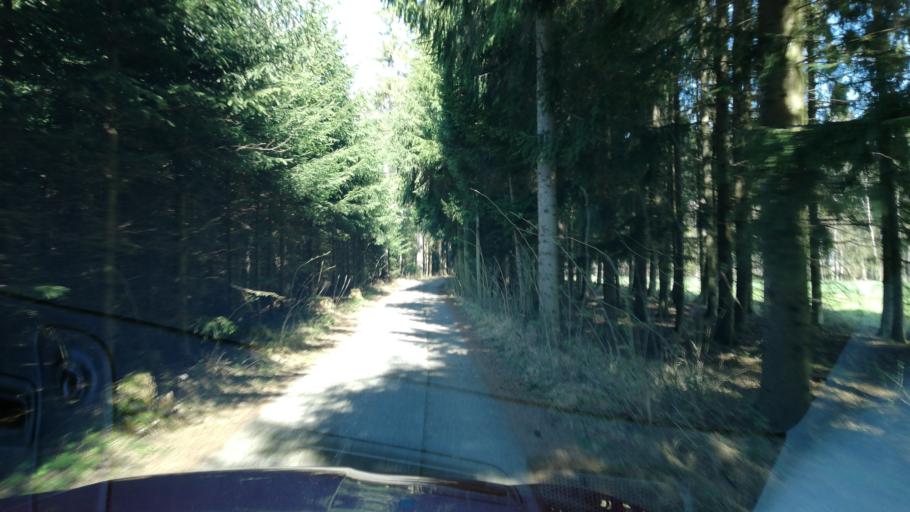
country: AT
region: Upper Austria
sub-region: Wels-Land
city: Sattledt
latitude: 48.0949
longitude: 14.0843
